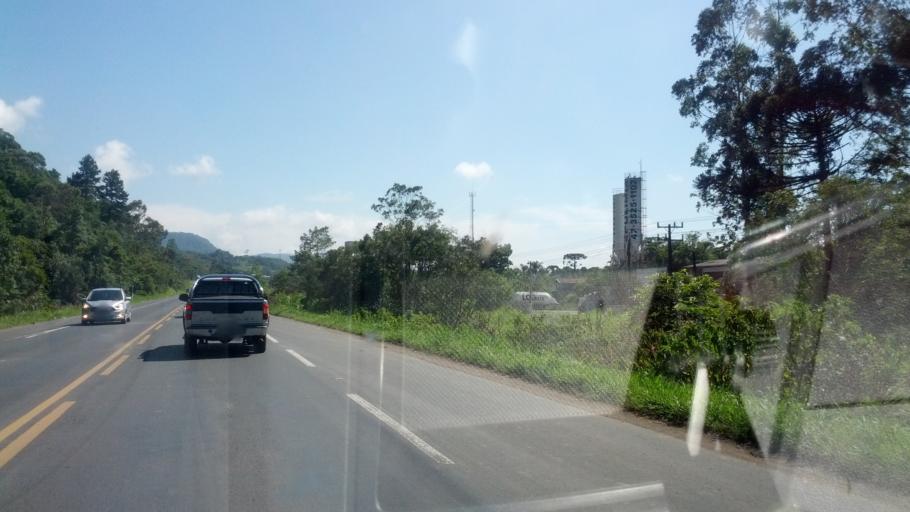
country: BR
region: Santa Catarina
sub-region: Rio Do Sul
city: Rio do Sul
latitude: -27.2312
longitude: -49.6705
